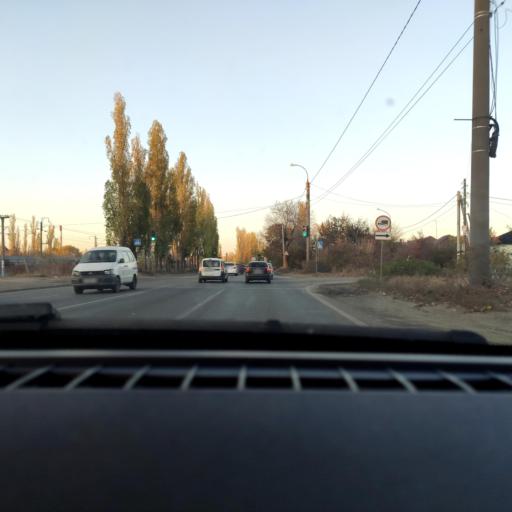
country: RU
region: Voronezj
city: Maslovka
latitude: 51.6166
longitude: 39.2584
